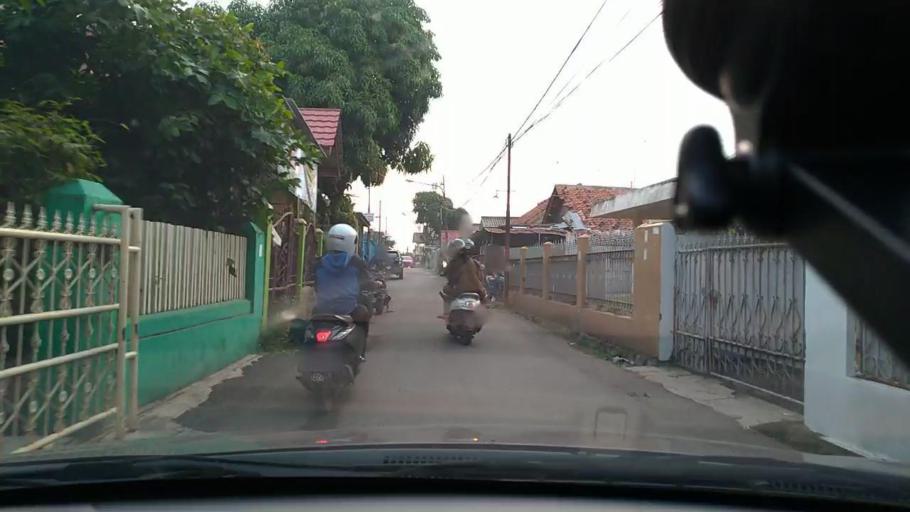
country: ID
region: West Java
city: Purwakarta
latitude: -6.5313
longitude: 107.4443
